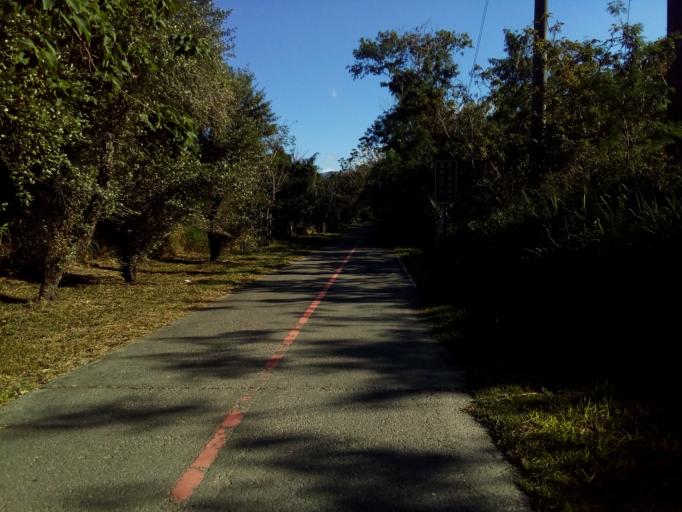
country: TW
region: Taiwan
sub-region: Taitung
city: Taitung
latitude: 23.0292
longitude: 121.1571
